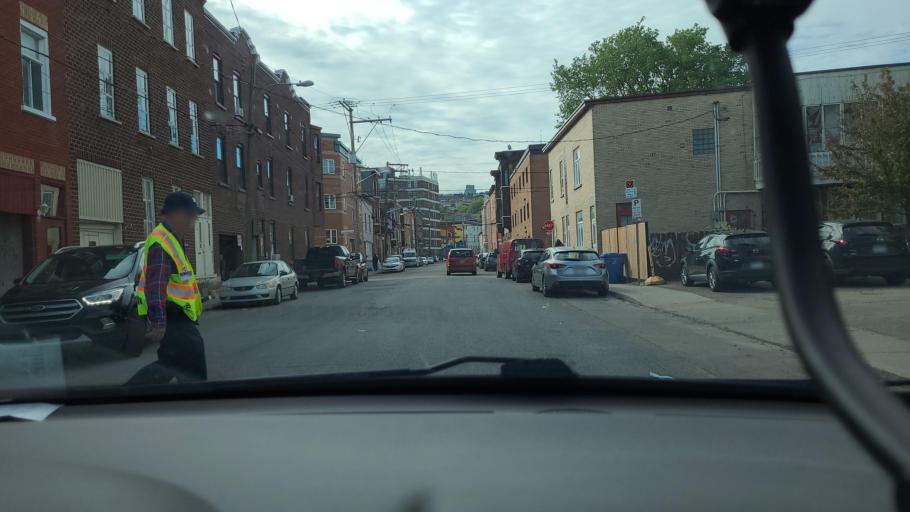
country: CA
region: Quebec
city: Quebec
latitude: 46.8149
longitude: -71.2304
